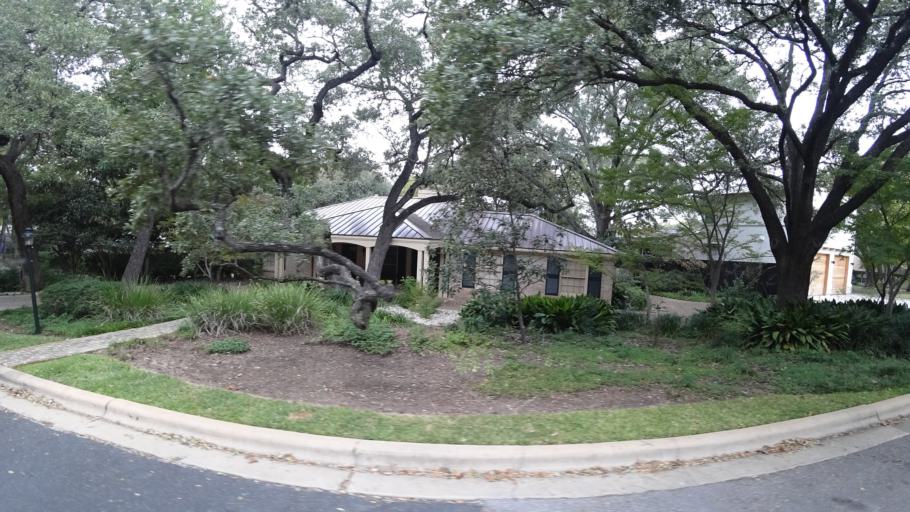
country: US
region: Texas
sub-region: Travis County
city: West Lake Hills
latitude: 30.3080
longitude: -97.7713
